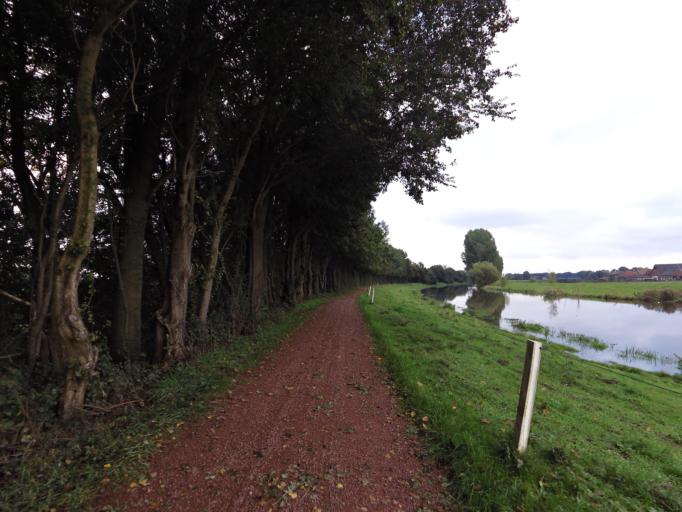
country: DE
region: North Rhine-Westphalia
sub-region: Regierungsbezirk Munster
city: Isselburg
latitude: 51.8490
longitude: 6.5195
